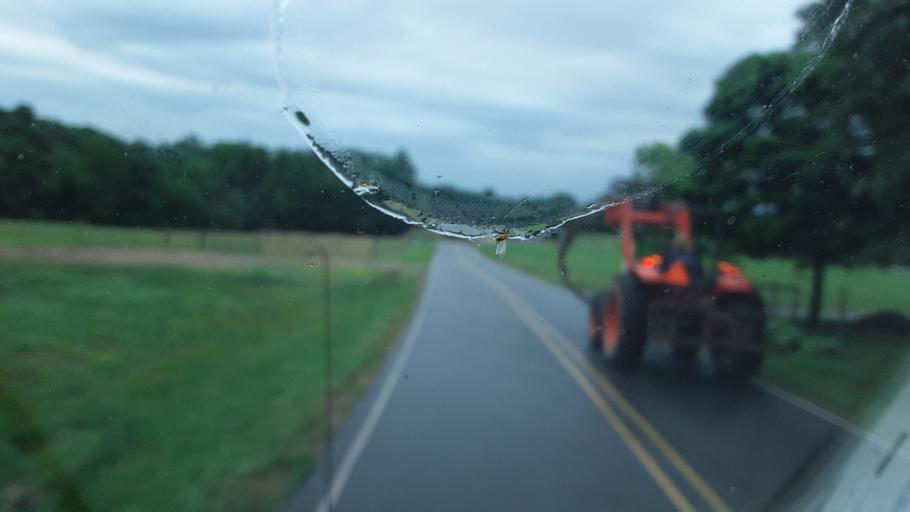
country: US
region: North Carolina
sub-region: Yadkin County
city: Jonesville
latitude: 36.0715
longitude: -80.8306
